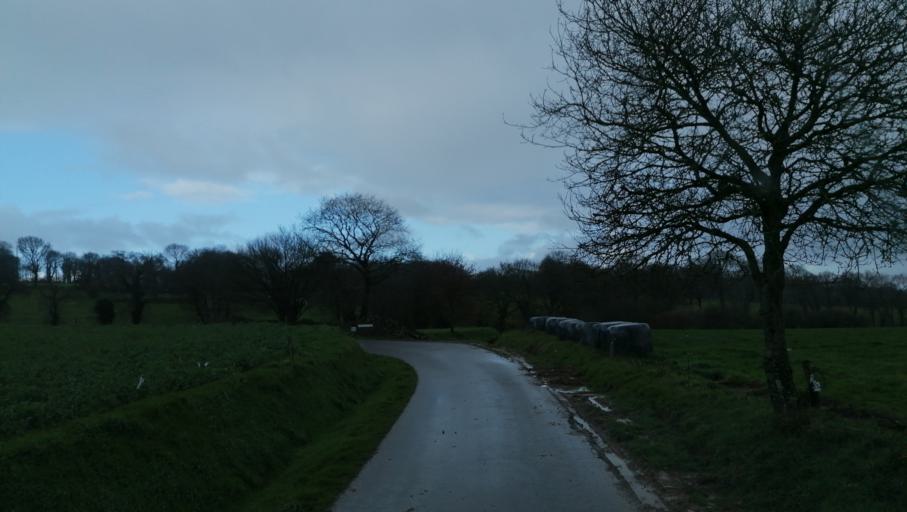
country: FR
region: Brittany
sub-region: Departement des Cotes-d'Armor
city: Plouagat
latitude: 48.4921
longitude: -2.9818
